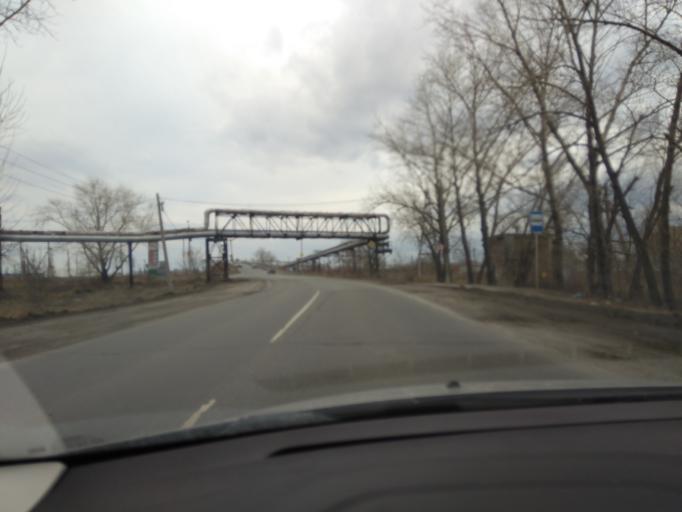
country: RU
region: Chelyabinsk
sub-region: Gorod Chelyabinsk
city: Chelyabinsk
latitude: 55.2499
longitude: 61.4555
